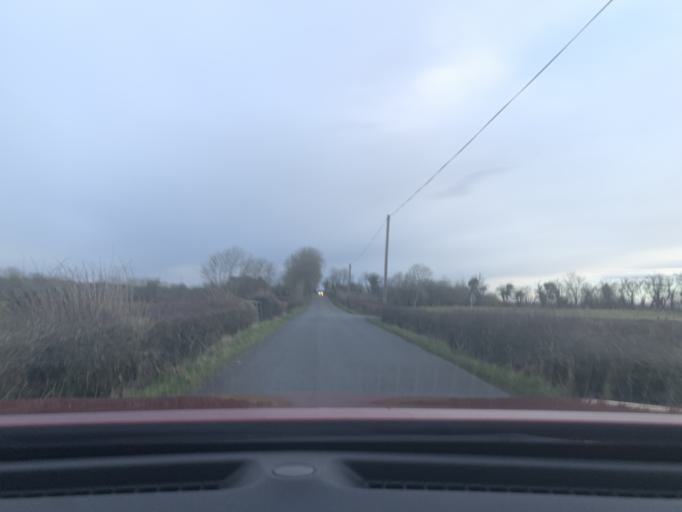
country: IE
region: Connaught
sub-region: Roscommon
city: Ballaghaderreen
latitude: 53.8733
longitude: -8.5583
